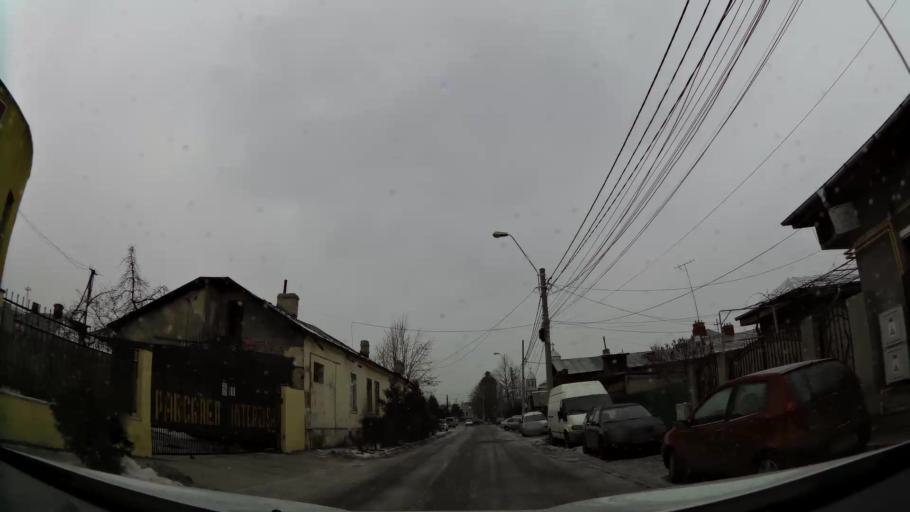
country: RO
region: Prahova
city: Ploiesti
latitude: 44.9412
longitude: 26.0409
